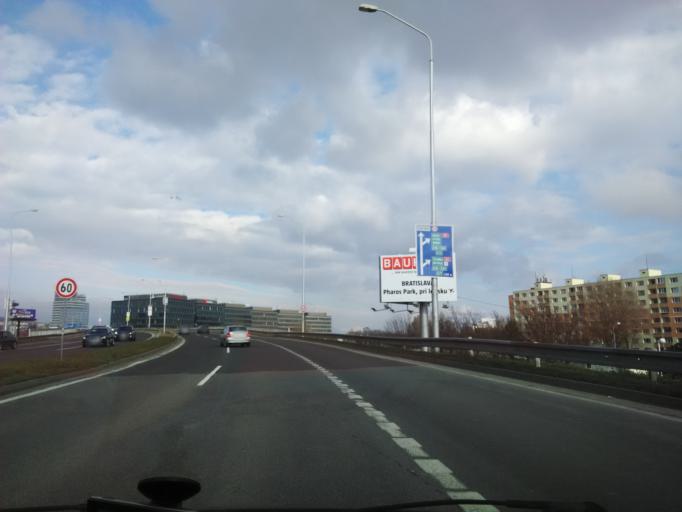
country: SK
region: Bratislavsky
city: Bratislava
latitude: 48.1256
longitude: 17.1046
